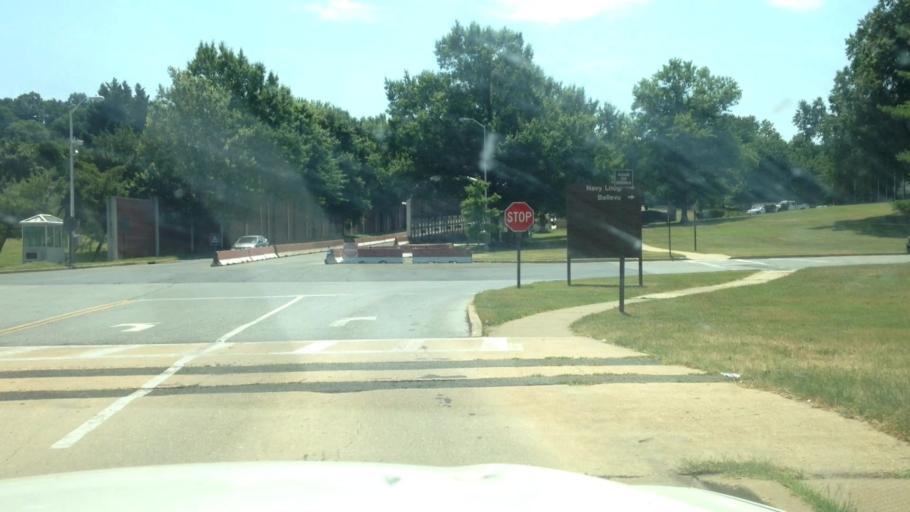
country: US
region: Maryland
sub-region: Prince George's County
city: Glassmanor
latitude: 38.8315
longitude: -77.0186
